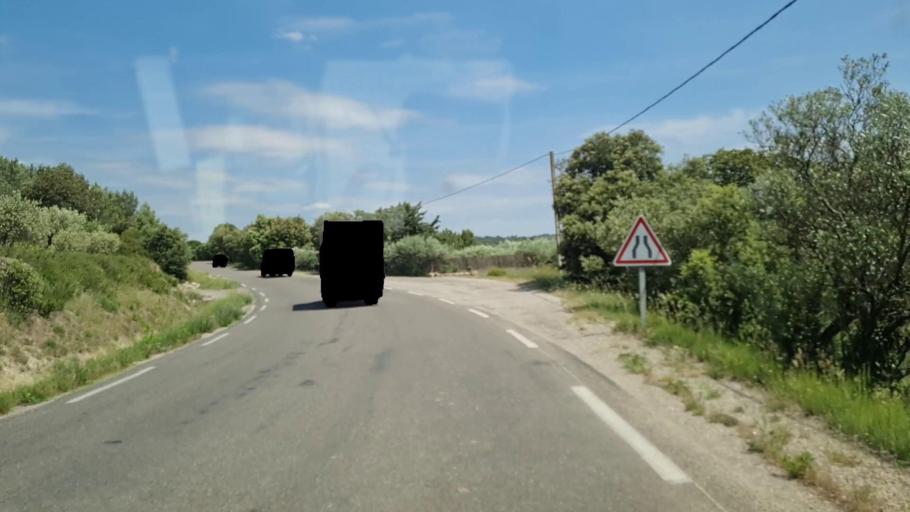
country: FR
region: Languedoc-Roussillon
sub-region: Departement du Gard
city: Cabrieres
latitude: 43.8918
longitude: 4.4735
